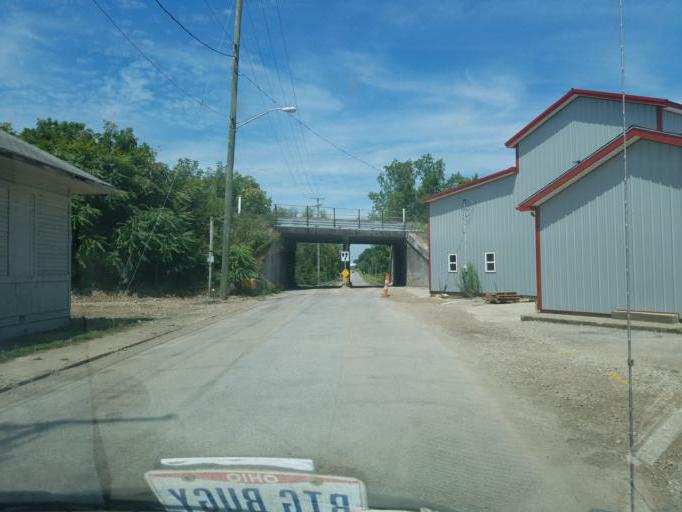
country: US
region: Ohio
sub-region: Madison County
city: West Jefferson
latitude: 39.9465
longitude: -83.2690
